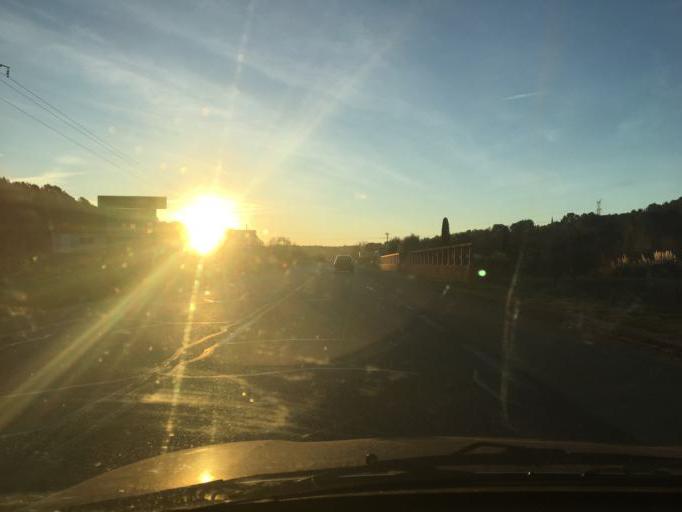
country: FR
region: Provence-Alpes-Cote d'Azur
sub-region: Departement du Var
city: Lorgues
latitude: 43.4728
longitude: 6.3787
